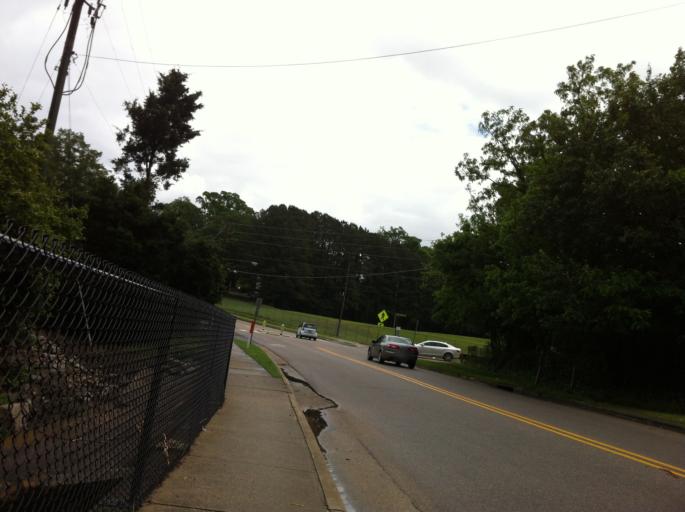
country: US
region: North Carolina
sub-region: Wake County
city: West Raleigh
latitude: 35.7787
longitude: -78.6633
